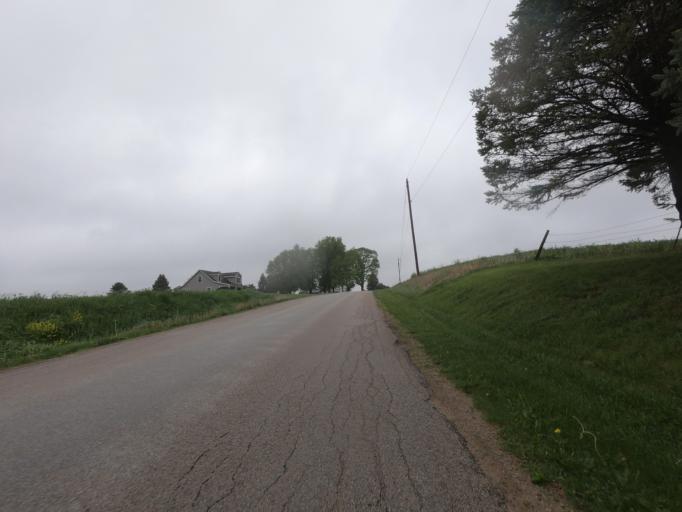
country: US
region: Wisconsin
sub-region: Grant County
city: Hazel Green
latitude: 42.4997
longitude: -90.5069
